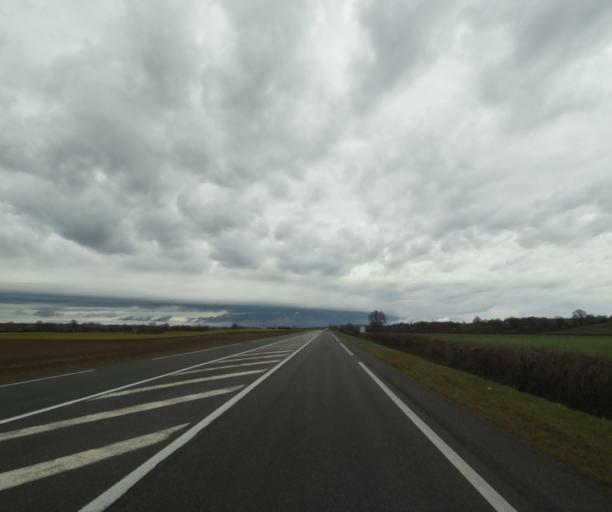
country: FR
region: Auvergne
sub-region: Departement de l'Allier
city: Bessay-sur-Allier
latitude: 46.4753
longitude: 3.3673
